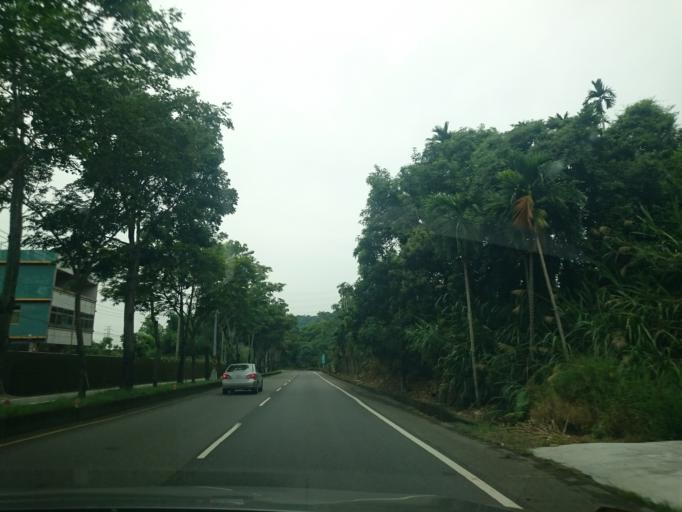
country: TW
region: Taiwan
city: Lugu
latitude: 23.8352
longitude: 120.7304
